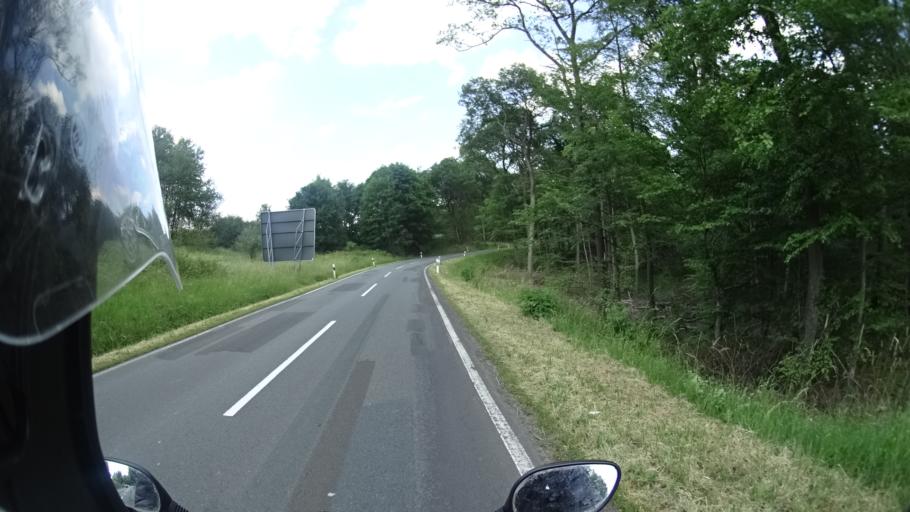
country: DE
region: Hesse
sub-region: Regierungsbezirk Darmstadt
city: Bad Schwalbach
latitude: 50.1247
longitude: 8.0840
